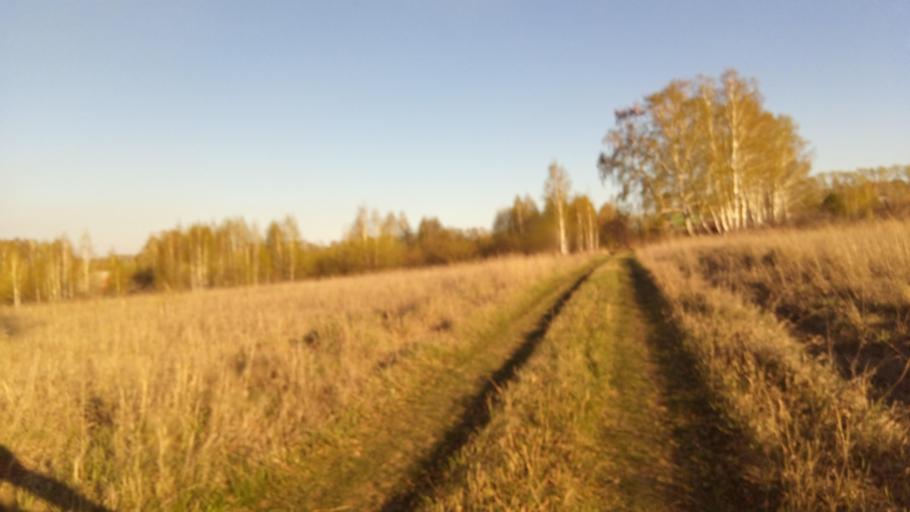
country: RU
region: Chelyabinsk
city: Timiryazevskiy
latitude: 54.9917
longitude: 60.8537
